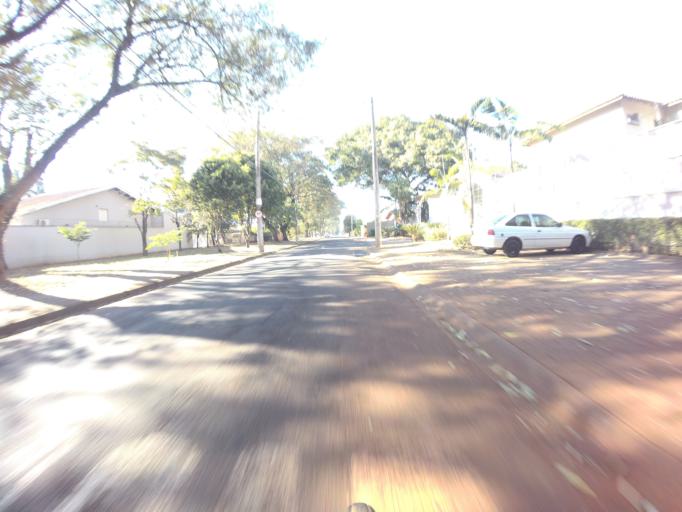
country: BR
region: Sao Paulo
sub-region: Piracicaba
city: Piracicaba
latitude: -22.7670
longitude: -47.5923
